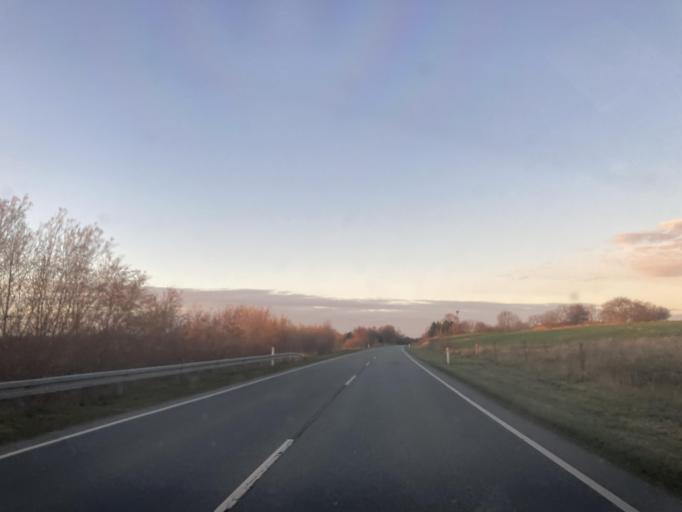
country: DK
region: Capital Region
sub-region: Gribskov Kommune
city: Graested
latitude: 56.0539
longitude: 12.2771
